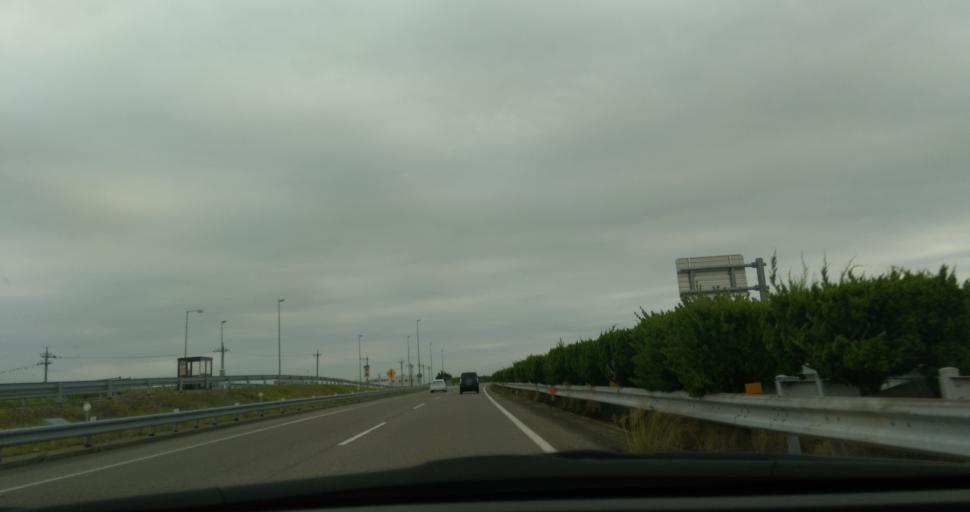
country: JP
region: Ishikawa
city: Matsuto
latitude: 36.5529
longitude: 136.5795
